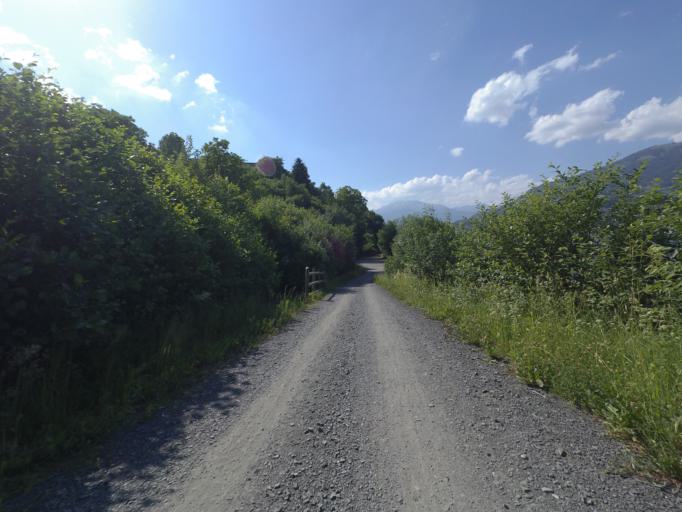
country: AT
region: Carinthia
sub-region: Politischer Bezirk Spittal an der Drau
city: Millstatt
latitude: 46.7919
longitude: 13.5742
